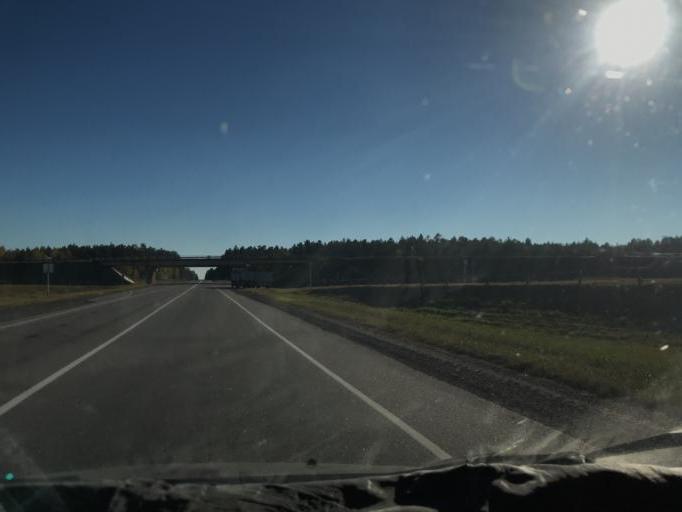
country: BY
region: Gomel
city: Kalinkavichy
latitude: 52.0751
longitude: 29.3610
